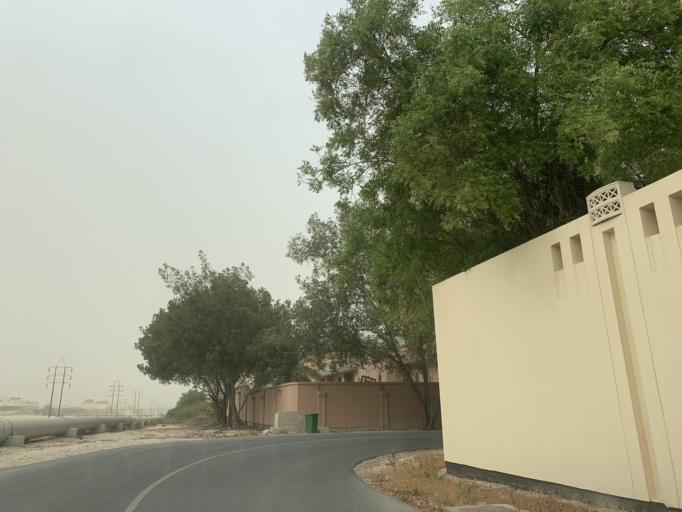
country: BH
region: Northern
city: Ar Rifa'
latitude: 26.1419
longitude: 50.5360
